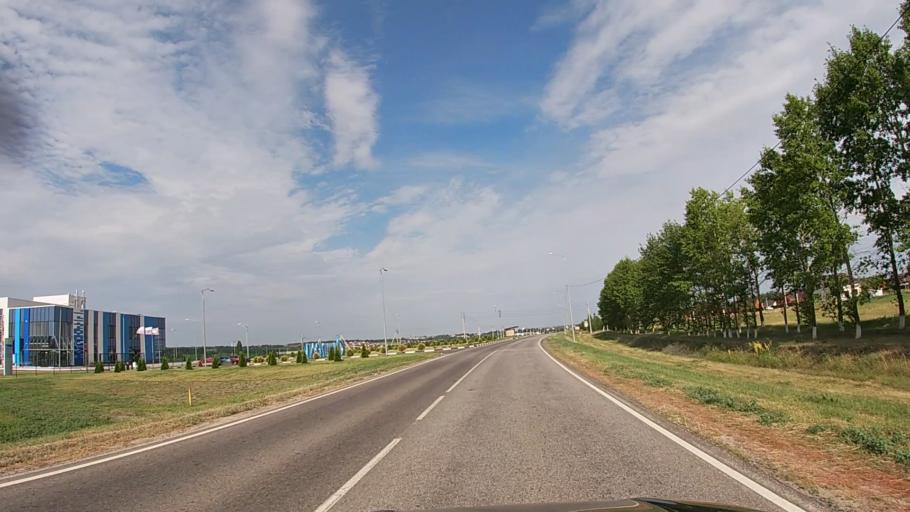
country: RU
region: Belgorod
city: Krasnaya Yaruga
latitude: 50.7964
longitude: 35.6930
